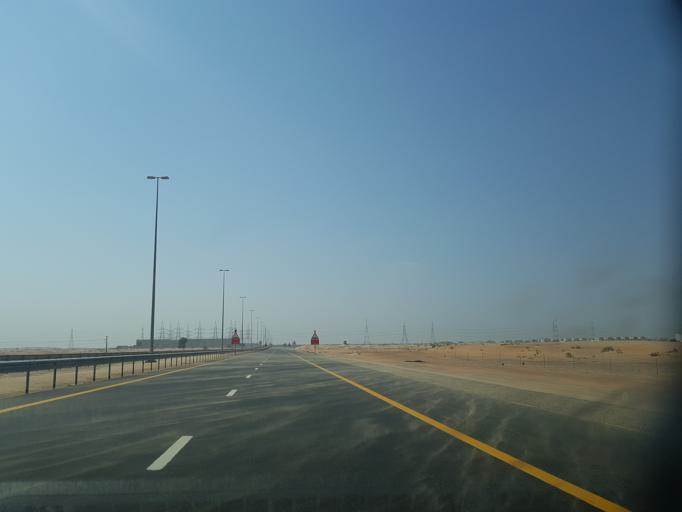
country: AE
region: Ash Shariqah
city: Sharjah
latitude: 25.2825
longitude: 55.6008
